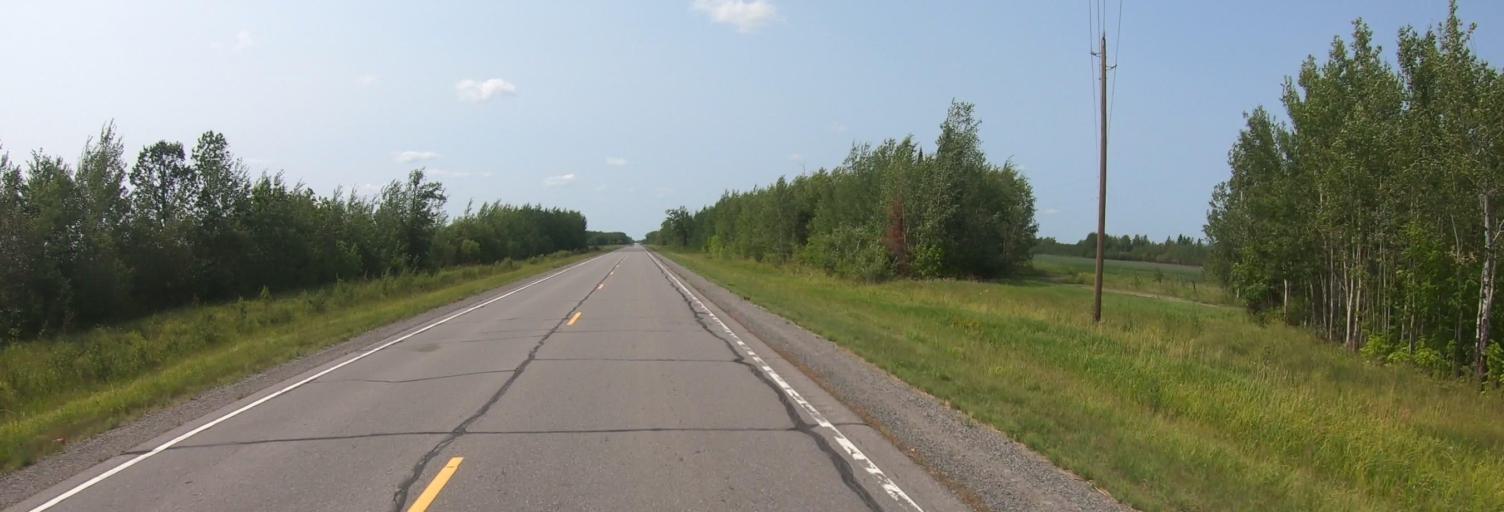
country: US
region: Minnesota
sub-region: Lake of the Woods County
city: Baudette
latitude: 48.6995
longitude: -94.3431
